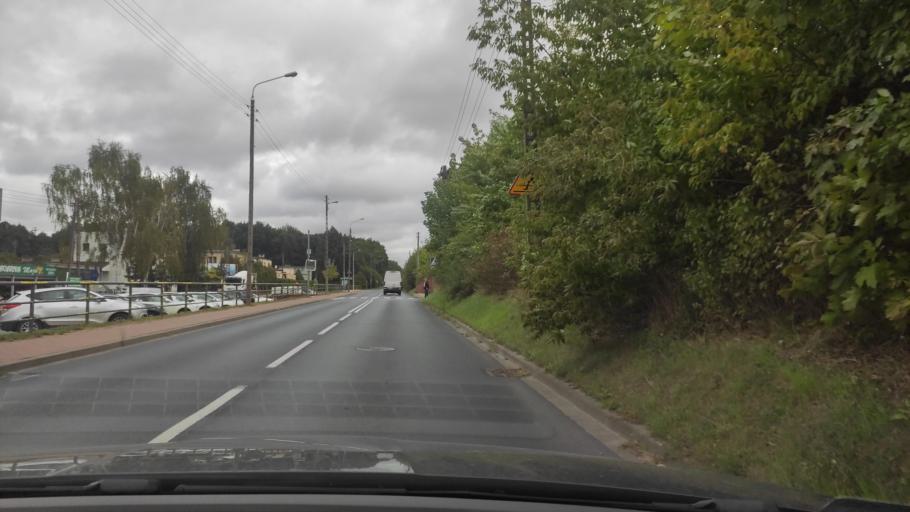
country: PL
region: Greater Poland Voivodeship
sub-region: Powiat poznanski
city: Czerwonak
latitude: 52.4248
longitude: 16.9926
